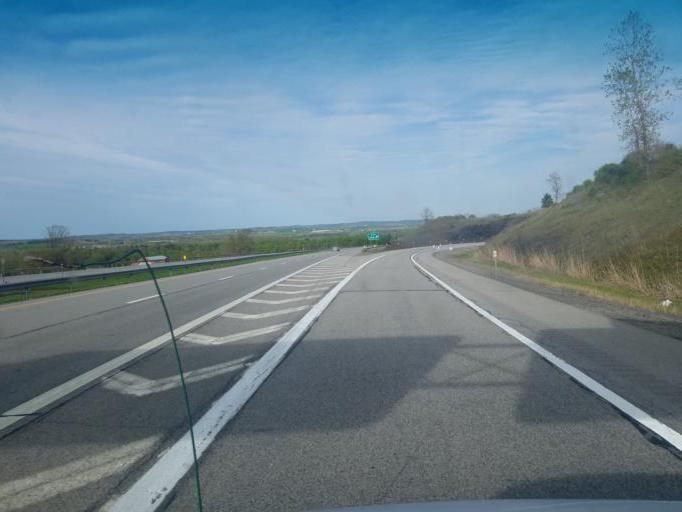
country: US
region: New York
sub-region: Herkimer County
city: Little Falls
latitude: 43.0155
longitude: -74.8236
